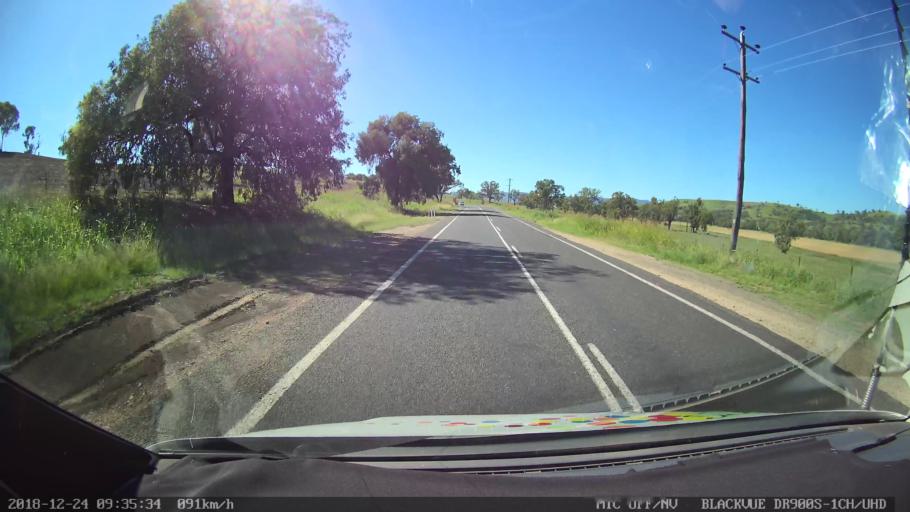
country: AU
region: New South Wales
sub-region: Liverpool Plains
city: Quirindi
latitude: -31.6309
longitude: 150.7181
